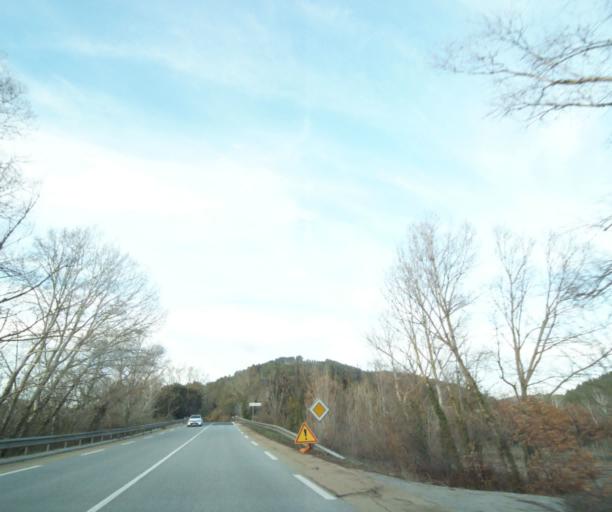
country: FR
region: Provence-Alpes-Cote d'Azur
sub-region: Departement du Var
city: La Motte
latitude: 43.4899
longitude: 6.5117
